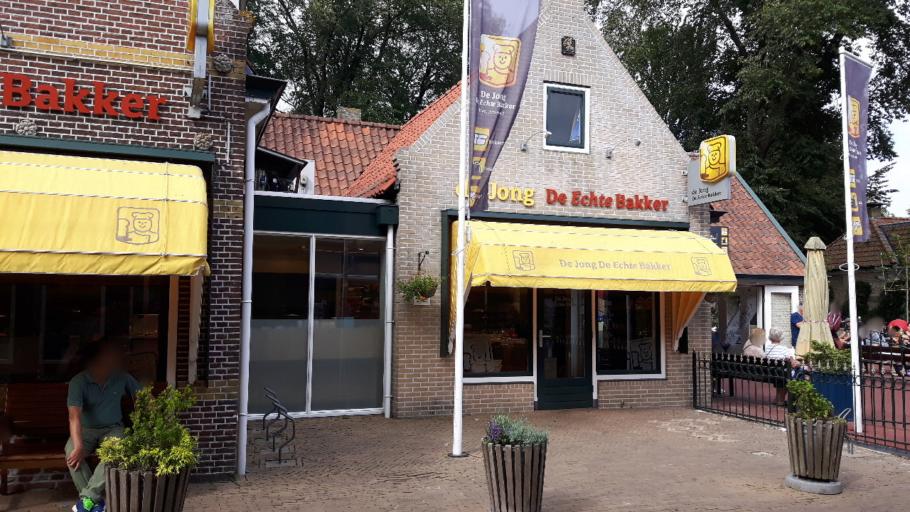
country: NL
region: Friesland
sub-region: Gemeente Ameland
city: Nes
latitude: 53.4452
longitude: 5.7724
